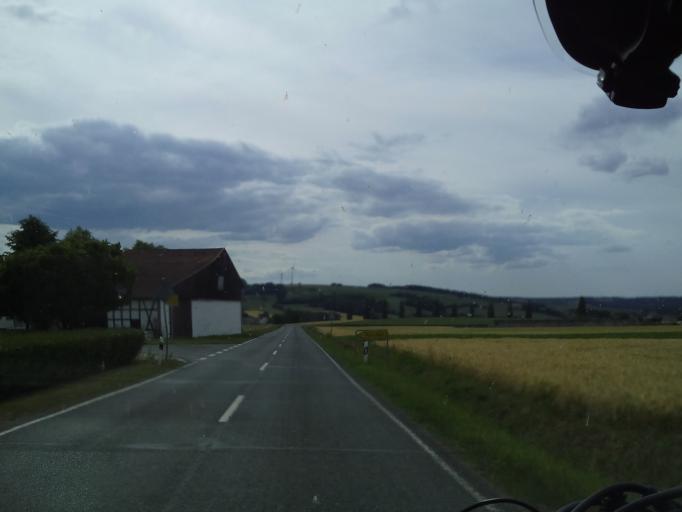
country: DE
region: Bavaria
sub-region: Regierungsbezirk Unterfranken
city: Untermerzbach
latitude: 50.1033
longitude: 10.8768
